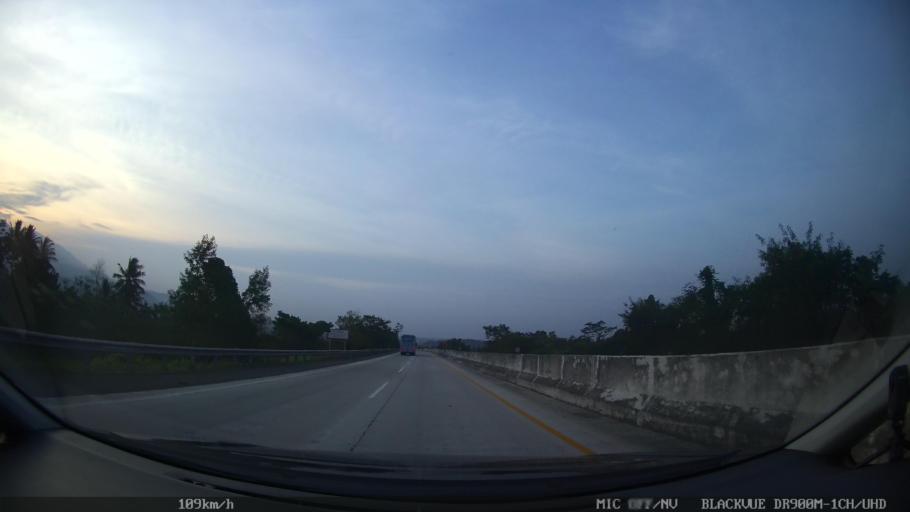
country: ID
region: Lampung
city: Penengahan
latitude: -5.7943
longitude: 105.7274
